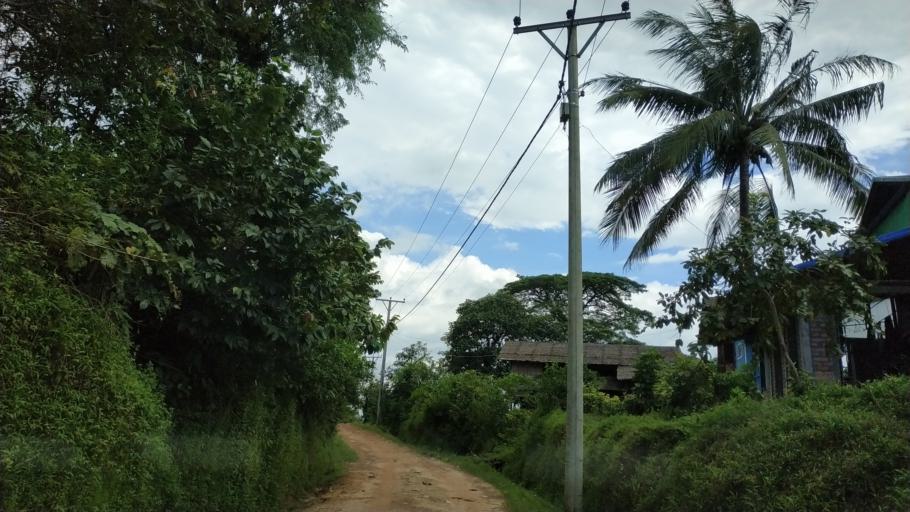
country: MM
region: Tanintharyi
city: Dawei
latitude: 14.1856
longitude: 98.1640
